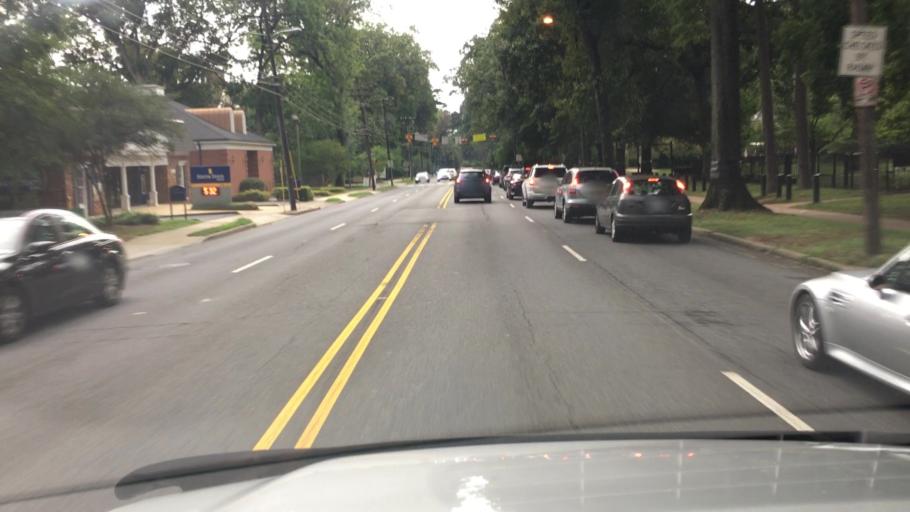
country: US
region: North Carolina
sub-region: Mecklenburg County
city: Charlotte
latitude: 35.1945
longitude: -80.8260
